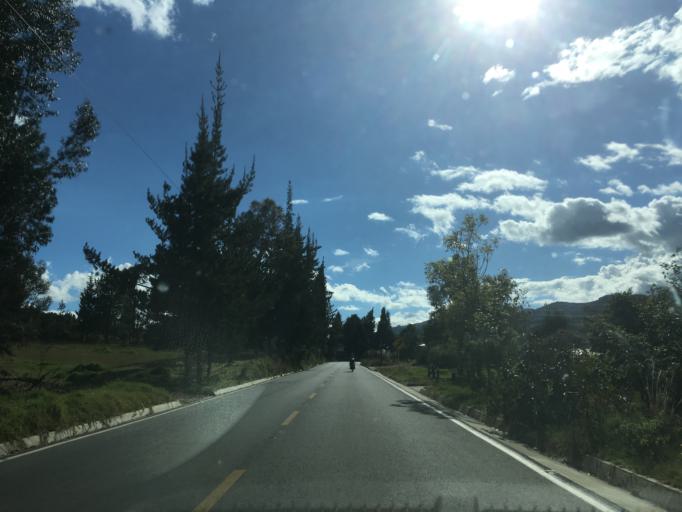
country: CO
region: Boyaca
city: Pesca
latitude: 5.6021
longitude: -73.0248
